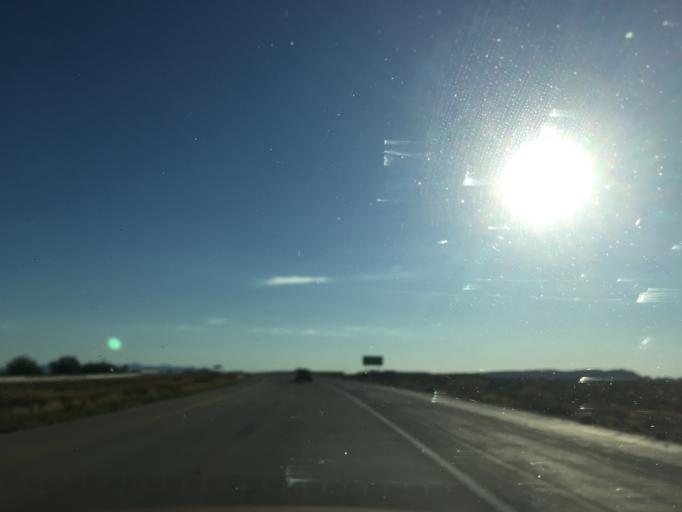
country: US
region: Arizona
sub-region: Maricopa County
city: Anthem
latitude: 33.7790
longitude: -112.2302
